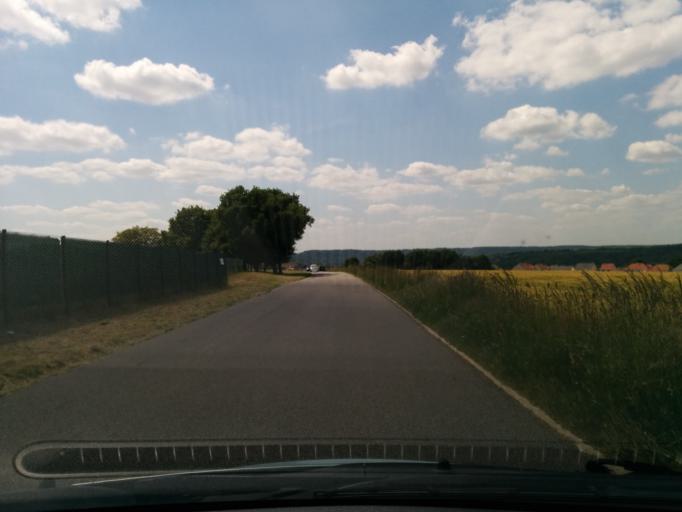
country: FR
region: Ile-de-France
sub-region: Departement des Yvelines
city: Freneuse
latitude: 49.0389
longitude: 1.6051
